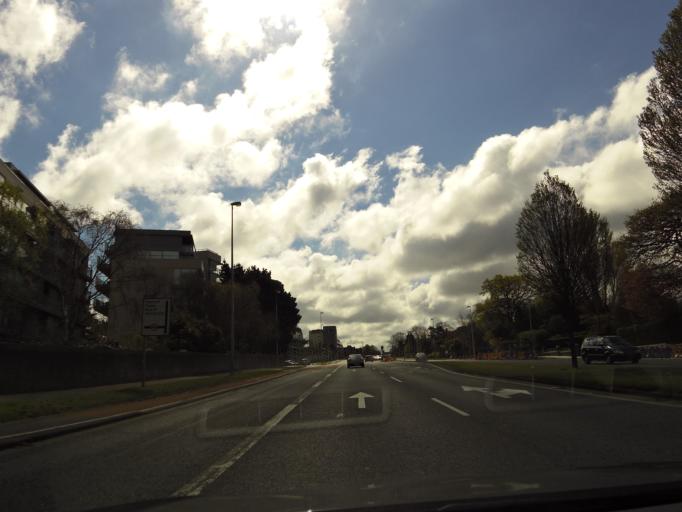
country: IE
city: Booterstown
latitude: 53.3008
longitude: -6.2052
